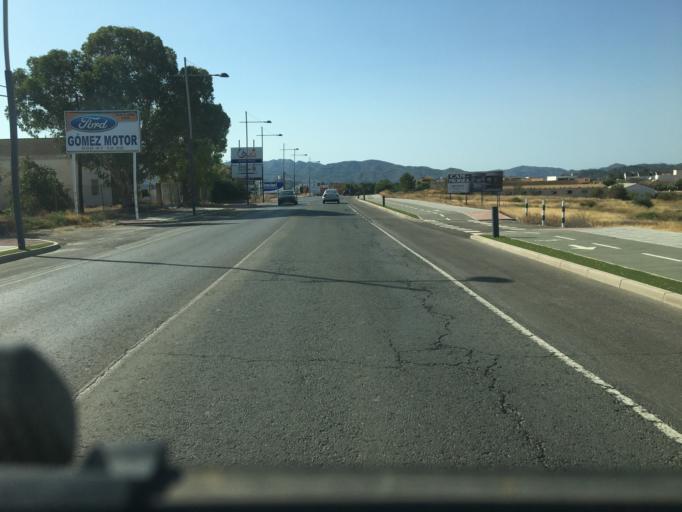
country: ES
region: Andalusia
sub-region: Provincia de Almeria
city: Huercal-Overa
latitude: 37.4061
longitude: -1.9570
